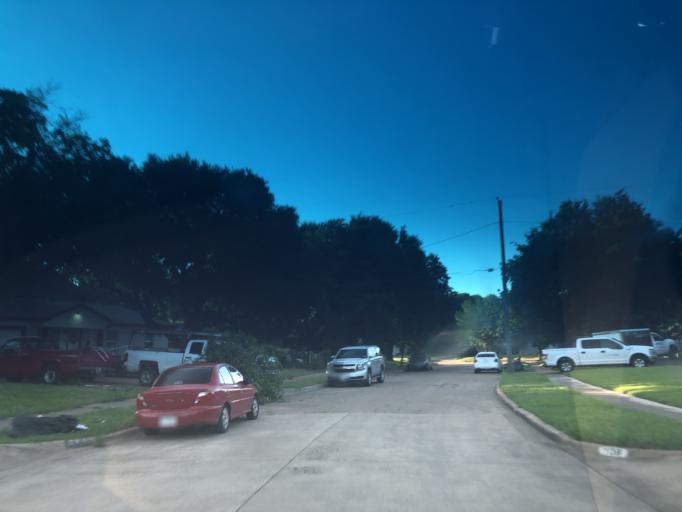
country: US
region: Texas
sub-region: Dallas County
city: Grand Prairie
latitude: 32.7057
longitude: -97.0136
